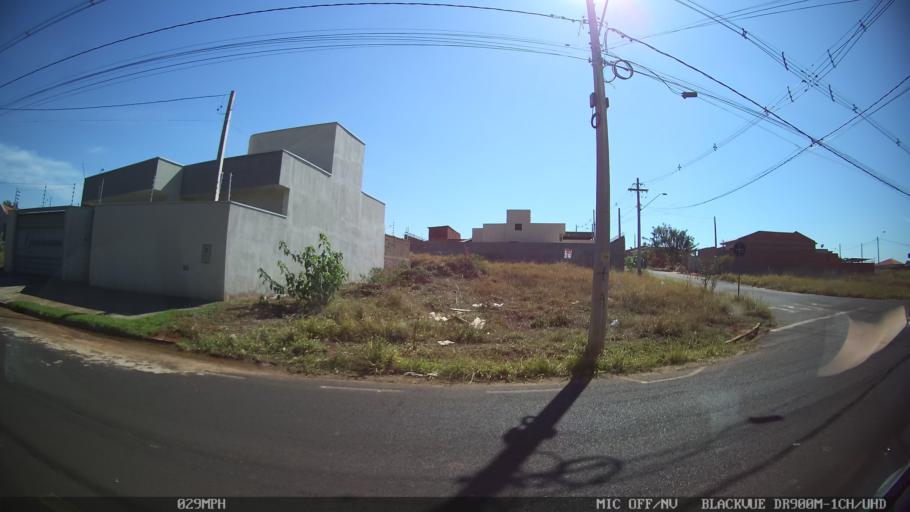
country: BR
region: Sao Paulo
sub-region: Sao Jose Do Rio Preto
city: Sao Jose do Rio Preto
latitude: -20.7605
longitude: -49.4214
